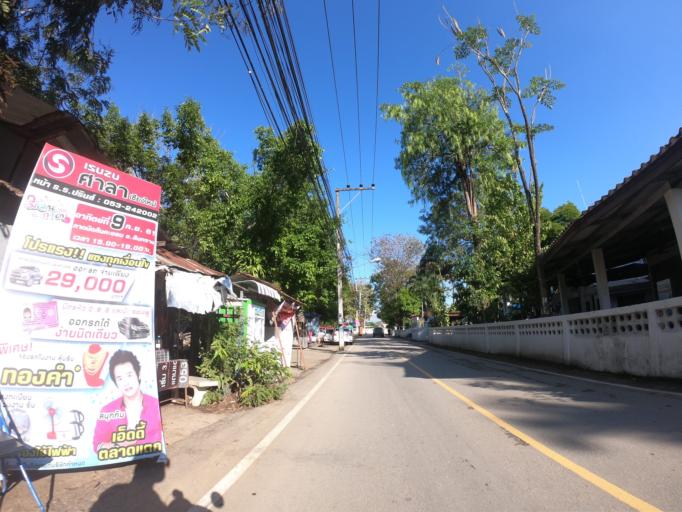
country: TH
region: Chiang Mai
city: San Sai
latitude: 18.8314
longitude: 99.0362
